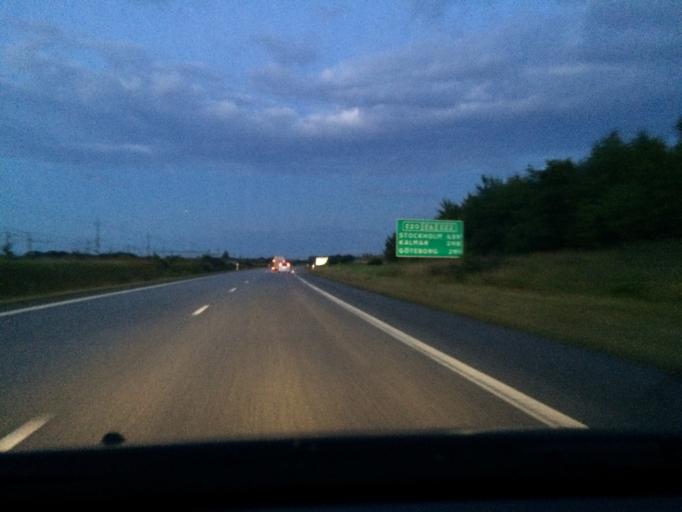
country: SE
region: Skane
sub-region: Malmo
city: Bunkeflostrand
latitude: 55.5641
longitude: 12.9249
